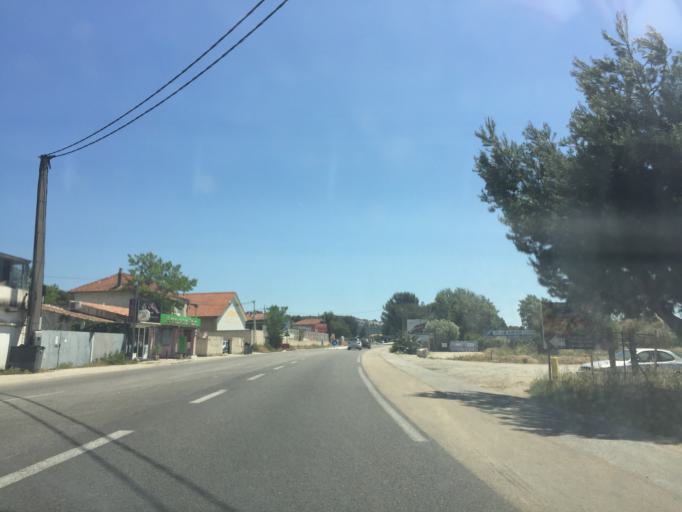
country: FR
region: Provence-Alpes-Cote d'Azur
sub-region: Departement des Bouches-du-Rhone
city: Rognac
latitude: 43.4846
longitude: 5.2234
